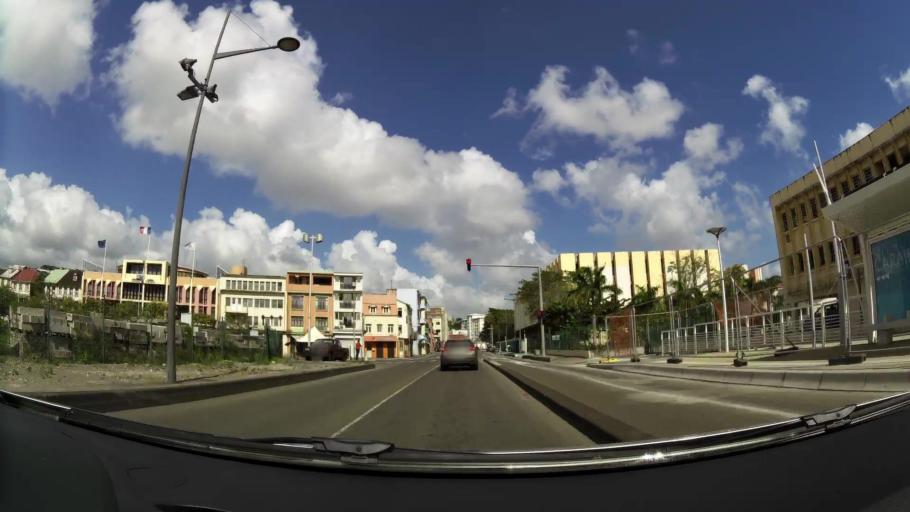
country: MQ
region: Martinique
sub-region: Martinique
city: Fort-de-France
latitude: 14.6034
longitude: -61.0661
